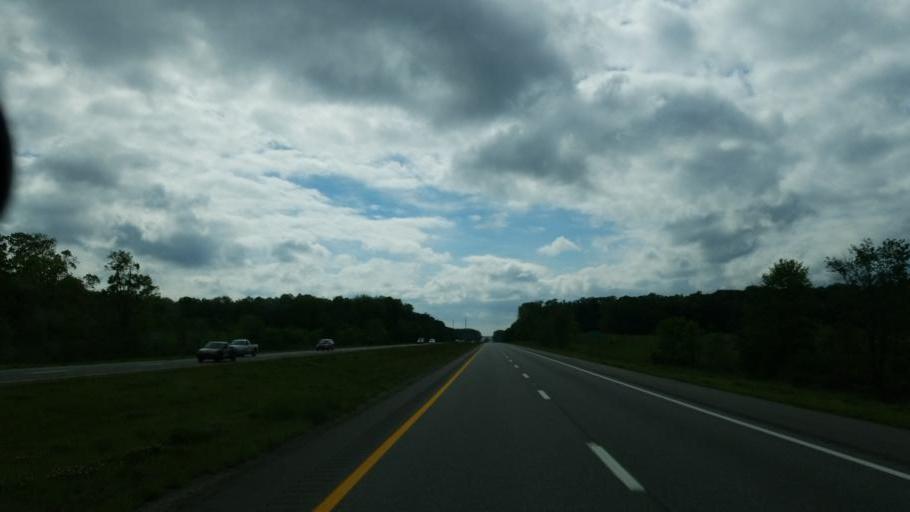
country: US
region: Ohio
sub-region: Geauga County
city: Bainbridge
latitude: 41.3814
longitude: -81.2886
